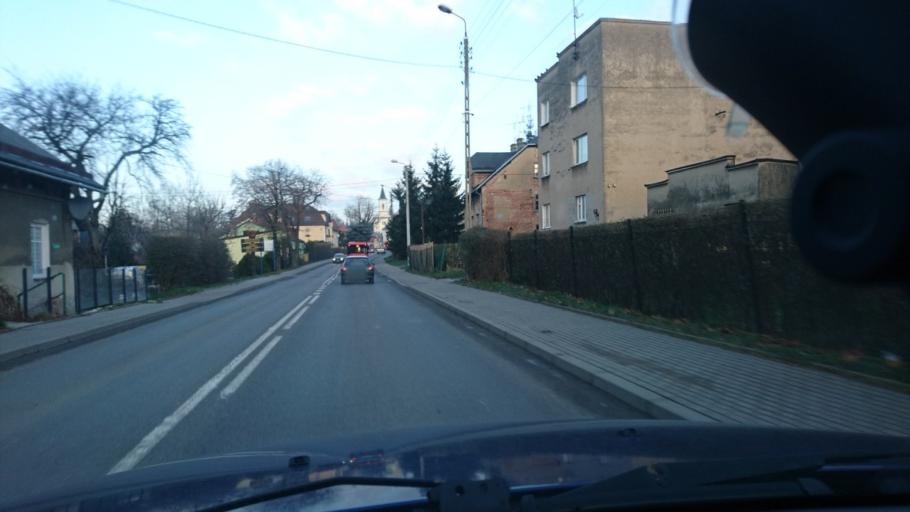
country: PL
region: Silesian Voivodeship
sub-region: Bielsko-Biala
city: Bielsko-Biala
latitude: 49.8178
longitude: 19.0817
